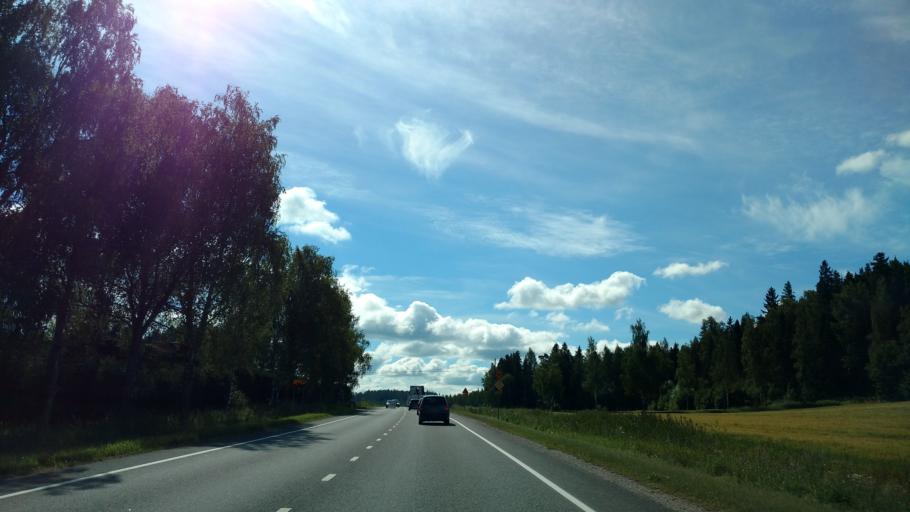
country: FI
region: Varsinais-Suomi
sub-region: Salo
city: Salo
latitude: 60.3685
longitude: 23.1363
